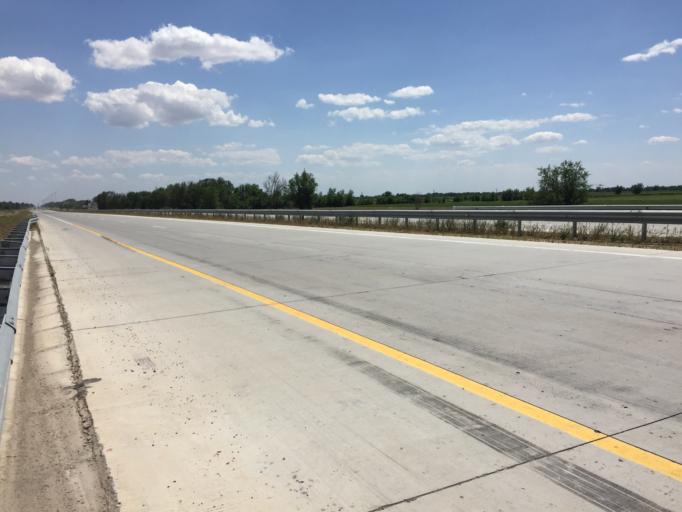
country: KZ
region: Ongtustik Qazaqstan
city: Shayan
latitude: 42.9112
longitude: 68.9786
